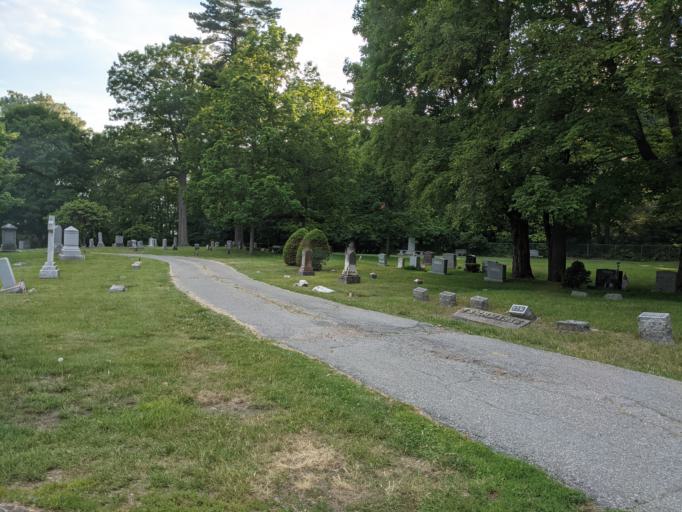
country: US
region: Vermont
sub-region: Chittenden County
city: Burlington
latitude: 44.4917
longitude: -73.2349
